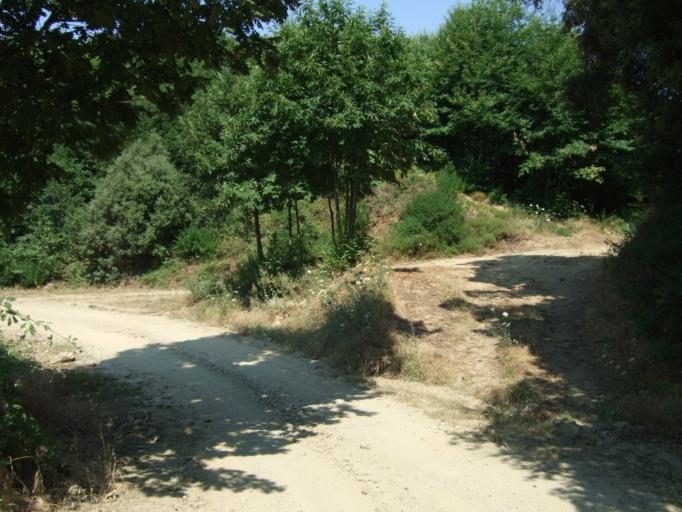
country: GR
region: Mount Athos
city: Karyes
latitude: 40.2700
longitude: 24.2234
